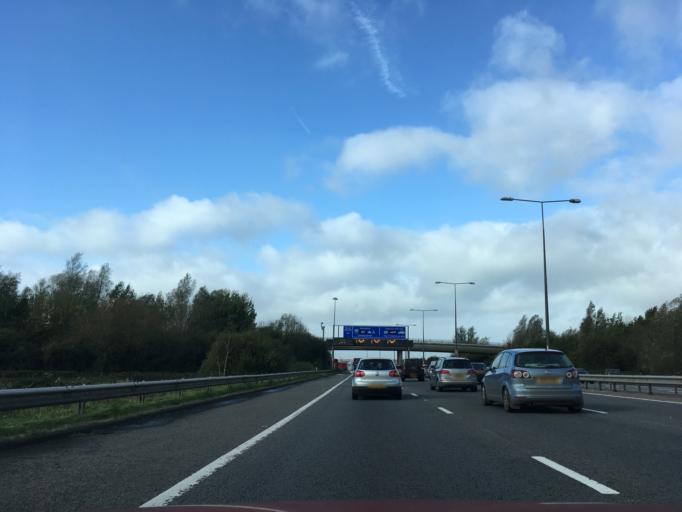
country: GB
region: Wales
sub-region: Monmouthshire
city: Rogiet
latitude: 51.5807
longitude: -2.7762
